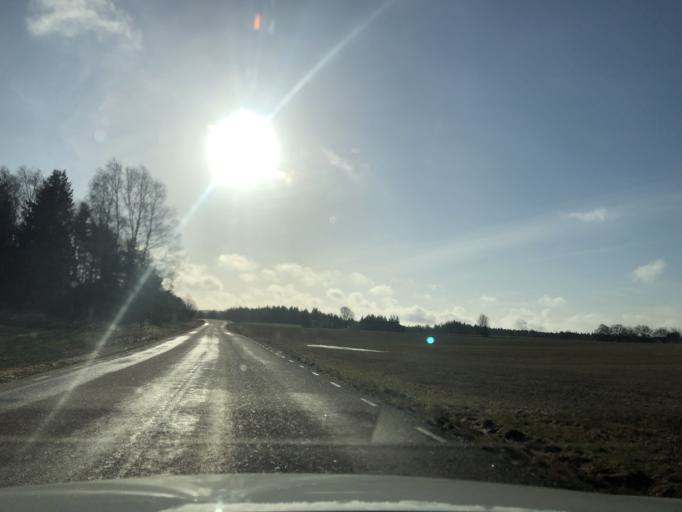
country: SE
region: Vaestra Goetaland
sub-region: Ulricehamns Kommun
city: Ulricehamn
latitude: 57.8169
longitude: 13.5329
